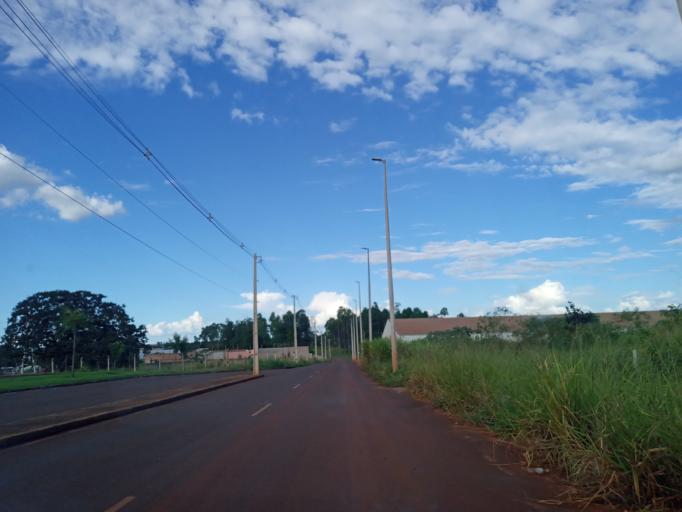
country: BR
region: Minas Gerais
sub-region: Ituiutaba
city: Ituiutaba
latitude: -18.9609
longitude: -49.4949
